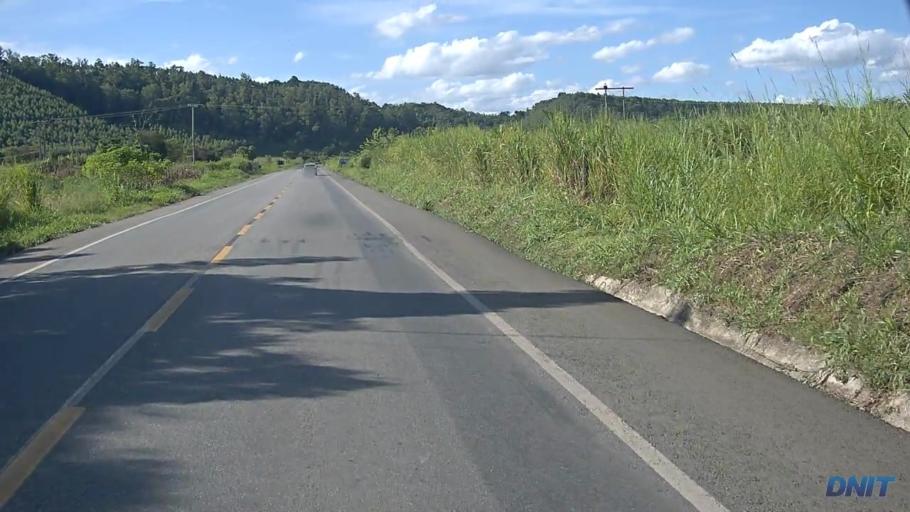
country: BR
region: Minas Gerais
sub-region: Belo Oriente
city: Belo Oriente
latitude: -19.2771
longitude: -42.3569
